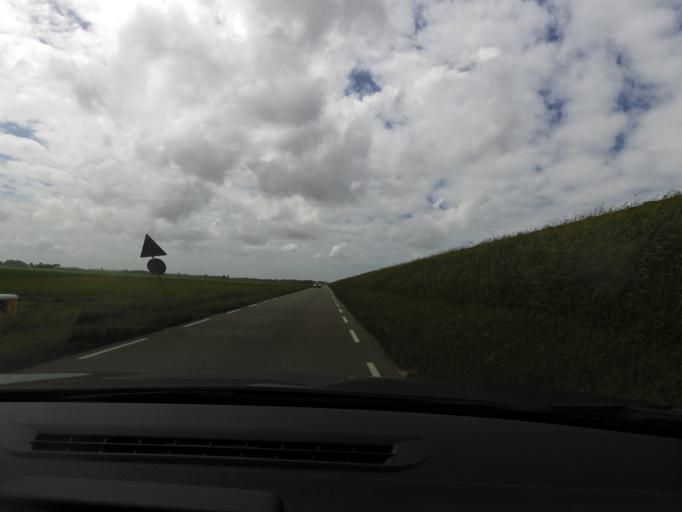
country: NL
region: Zeeland
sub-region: Schouwen-Duiveland
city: Scharendijke
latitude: 51.7421
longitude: 3.8782
